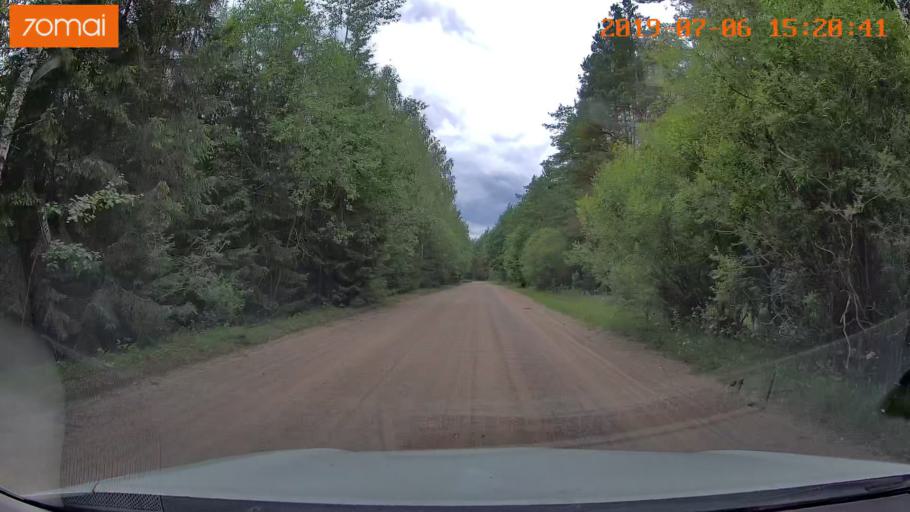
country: BY
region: Minsk
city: Valozhyn
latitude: 54.0076
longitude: 26.6300
